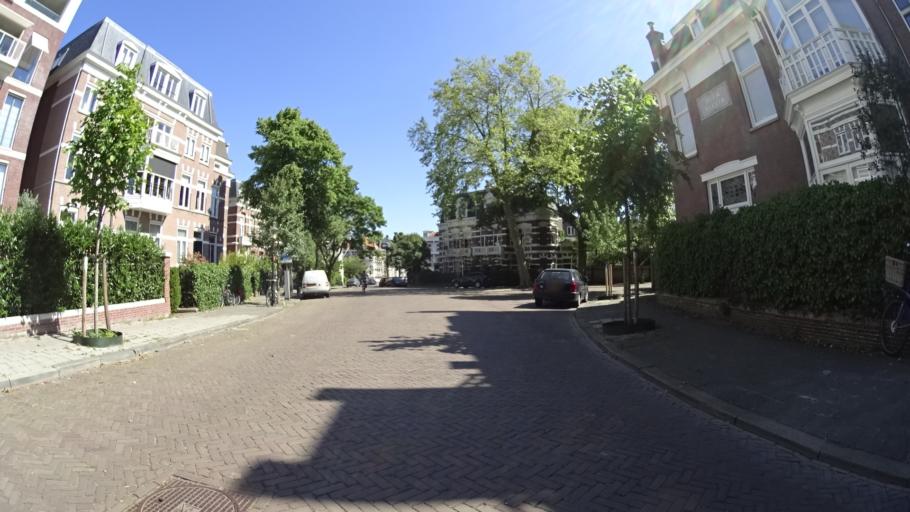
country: NL
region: South Holland
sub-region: Gemeente Den Haag
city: The Hague
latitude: 52.0924
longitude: 4.2979
